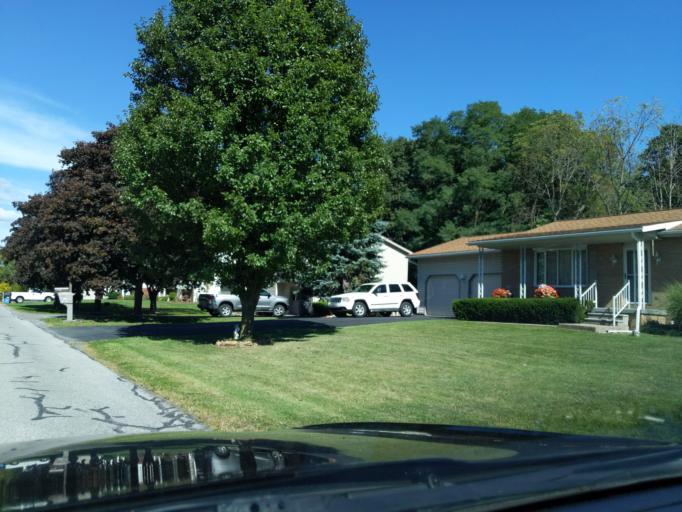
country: US
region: Pennsylvania
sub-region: Blair County
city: Greenwood
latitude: 40.5372
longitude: -78.3625
